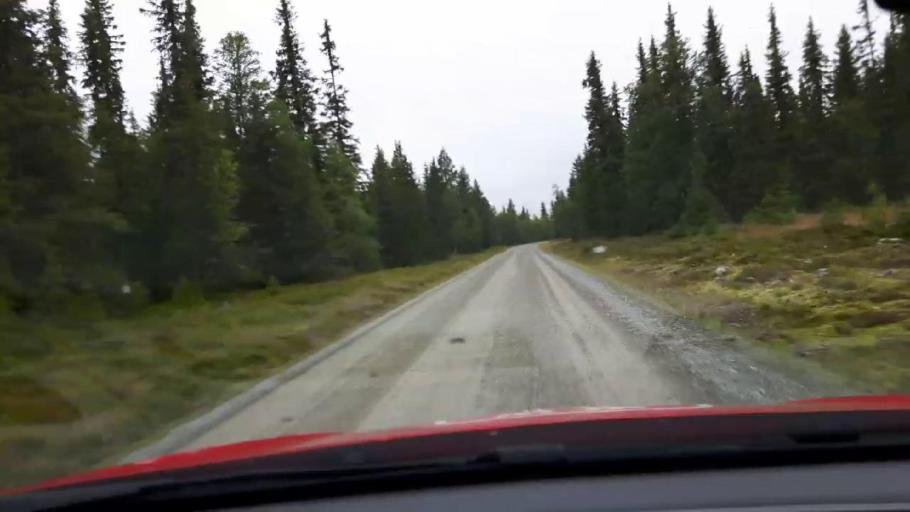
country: SE
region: Jaemtland
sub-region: Bergs Kommun
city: Hoverberg
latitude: 62.8606
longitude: 13.9449
